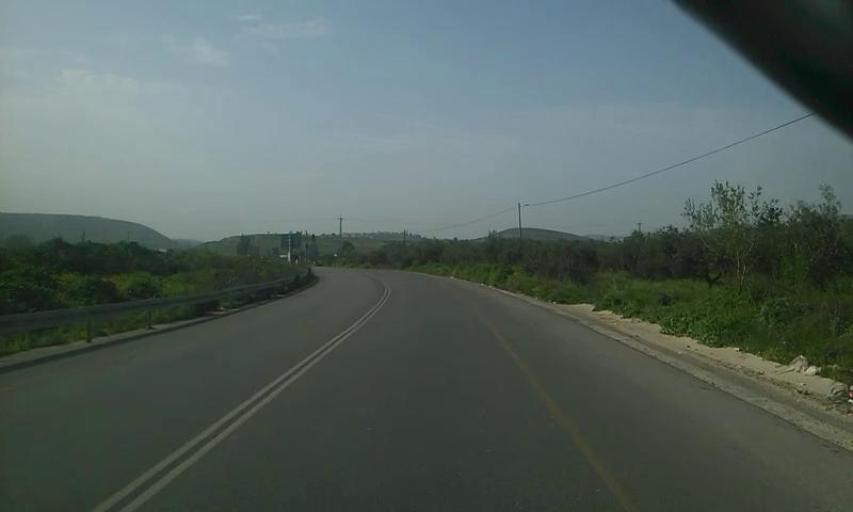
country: PS
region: West Bank
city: Dayr Sharaf
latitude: 32.2630
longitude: 35.1726
